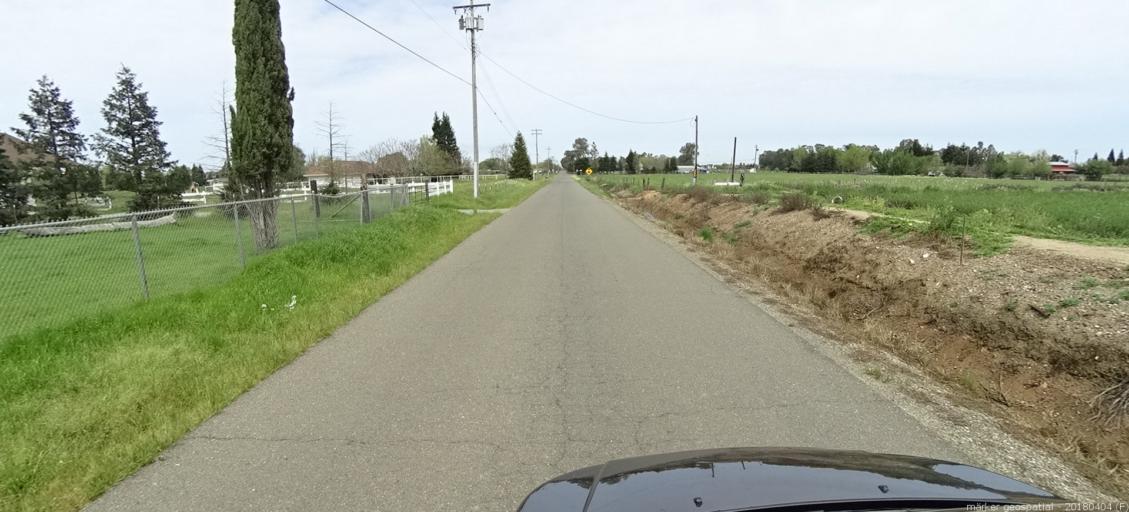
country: US
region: California
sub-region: Sacramento County
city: Herald
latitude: 38.2753
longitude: -121.2359
